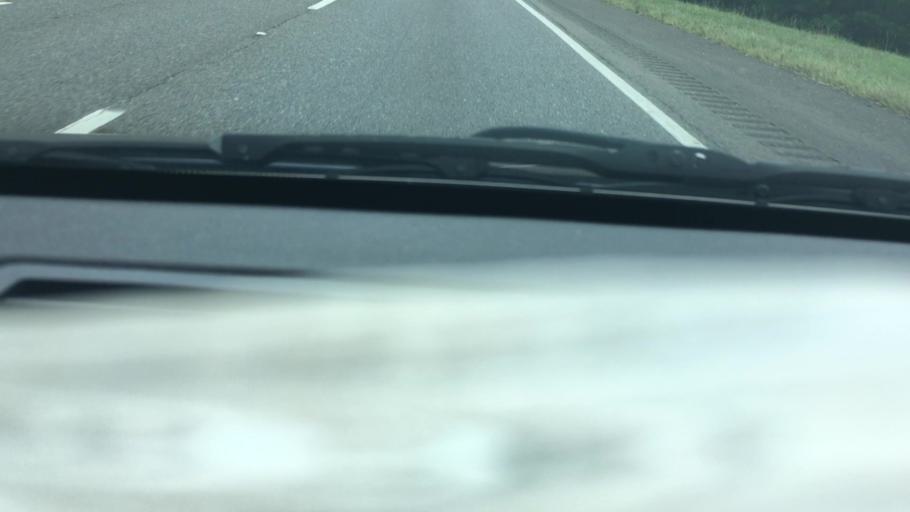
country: US
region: Alabama
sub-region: Pickens County
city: Gordo
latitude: 33.2724
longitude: -87.7509
